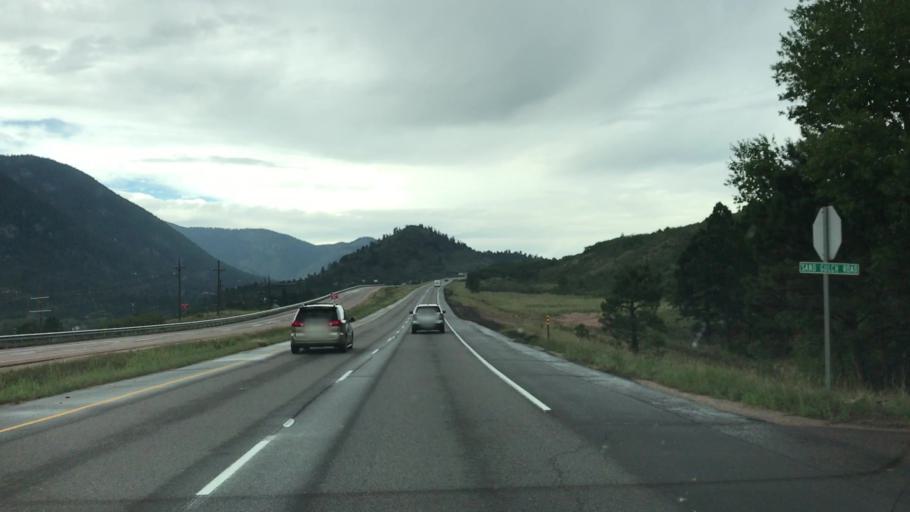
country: US
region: Colorado
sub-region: El Paso County
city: Cascade-Chipita Park
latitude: 38.9223
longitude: -104.9911
